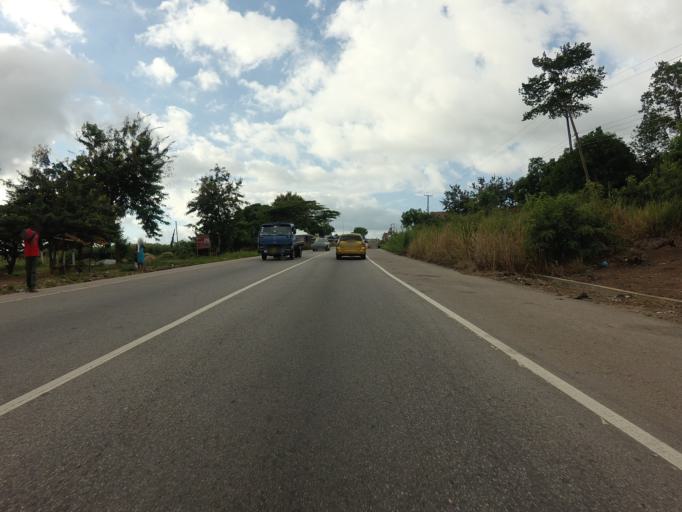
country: GH
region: Ashanti
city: Tafo
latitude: 6.8343
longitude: -1.6506
